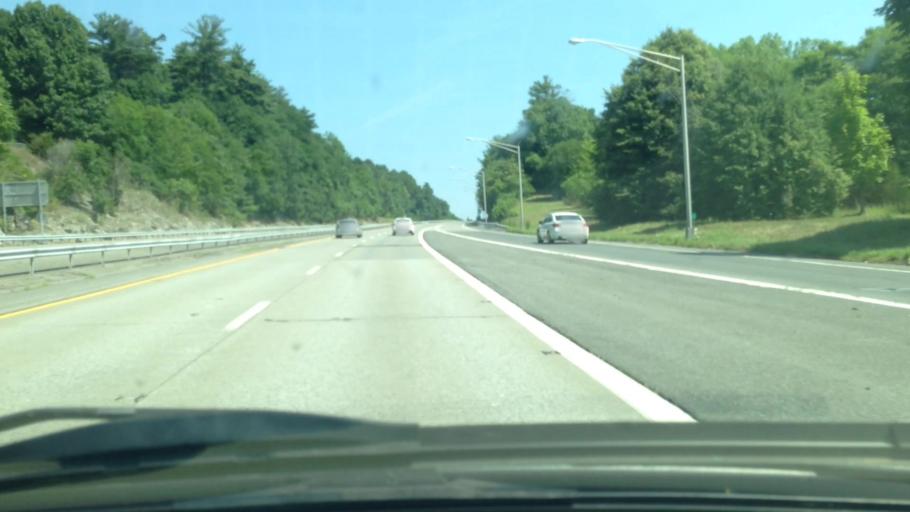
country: US
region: New York
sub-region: Ulster County
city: Kingston
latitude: 41.9295
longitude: -73.9857
